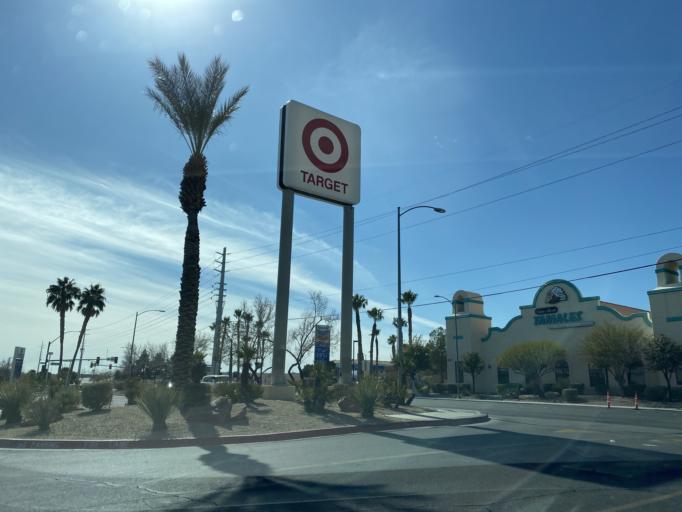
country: US
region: Nevada
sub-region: Clark County
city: Spring Valley
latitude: 36.2194
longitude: -115.2510
